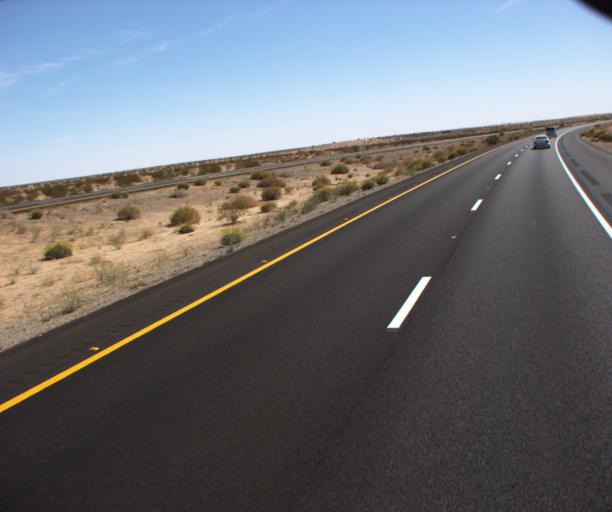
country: US
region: Arizona
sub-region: Yuma County
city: Fortuna Foothills
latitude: 32.6215
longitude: -114.5210
